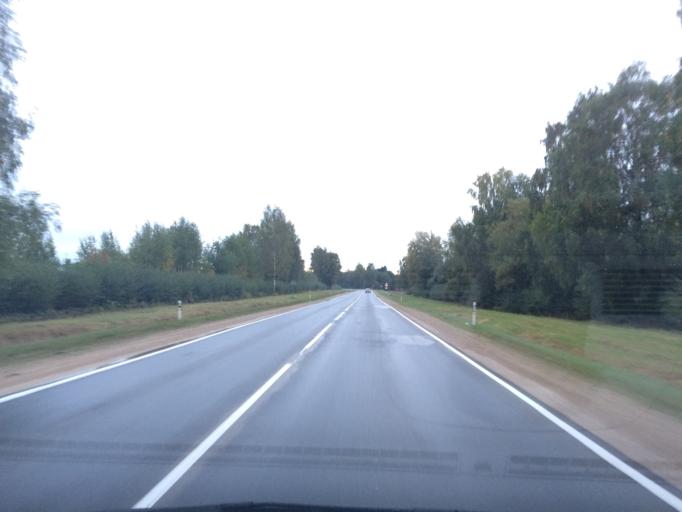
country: LV
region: Salas
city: Sala
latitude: 56.5534
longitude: 25.7943
